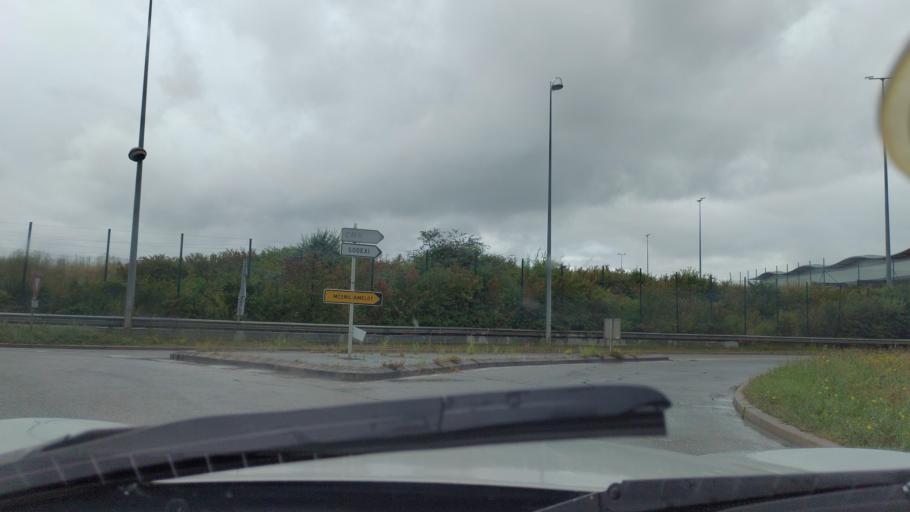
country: FR
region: Ile-de-France
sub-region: Departement de Seine-et-Marne
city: Mitry-Mory
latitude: 49.0107
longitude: 2.5994
